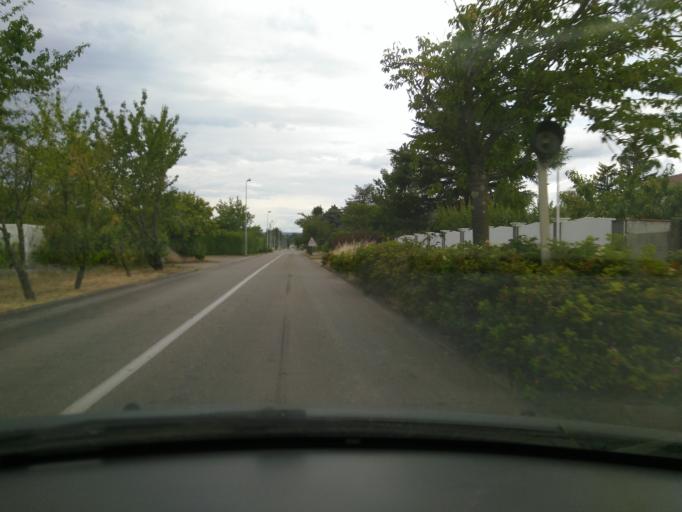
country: FR
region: Rhone-Alpes
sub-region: Departement de l'Isere
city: Beaurepaire
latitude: 45.3489
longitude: 5.0395
